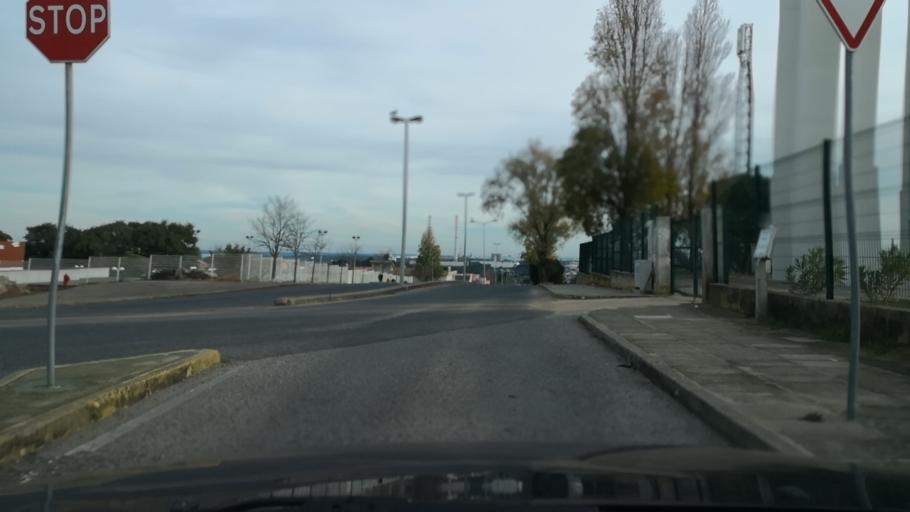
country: PT
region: Setubal
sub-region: Setubal
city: Setubal
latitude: 38.5210
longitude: -8.8721
